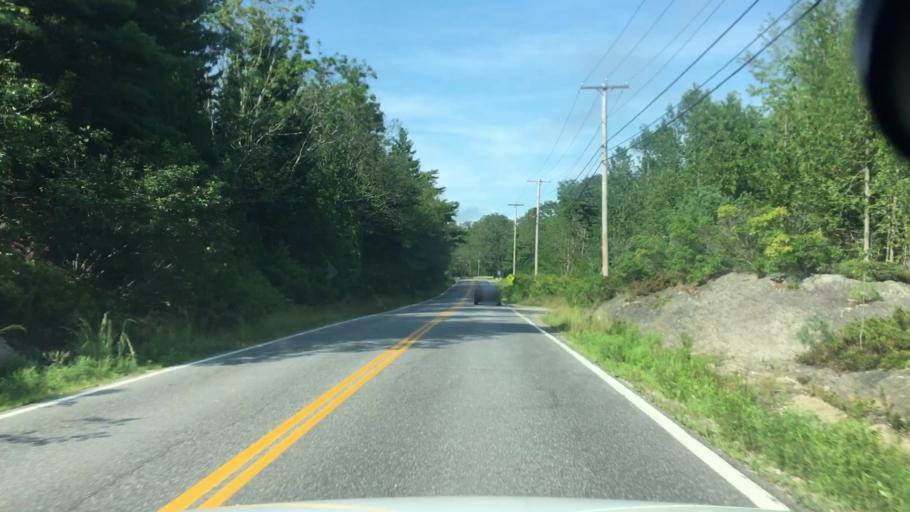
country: US
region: Maine
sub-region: Cumberland County
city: Harpswell Center
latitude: 43.7852
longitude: -69.9498
